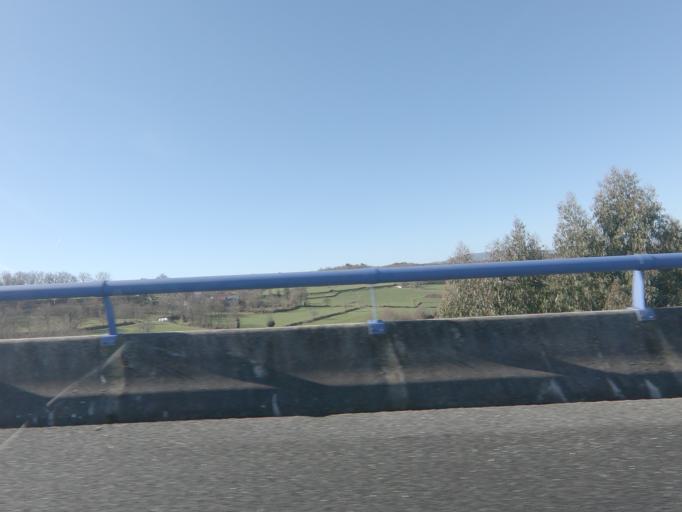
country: ES
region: Galicia
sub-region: Provincia de Pontevedra
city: Lalin
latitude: 42.6283
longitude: -8.1181
